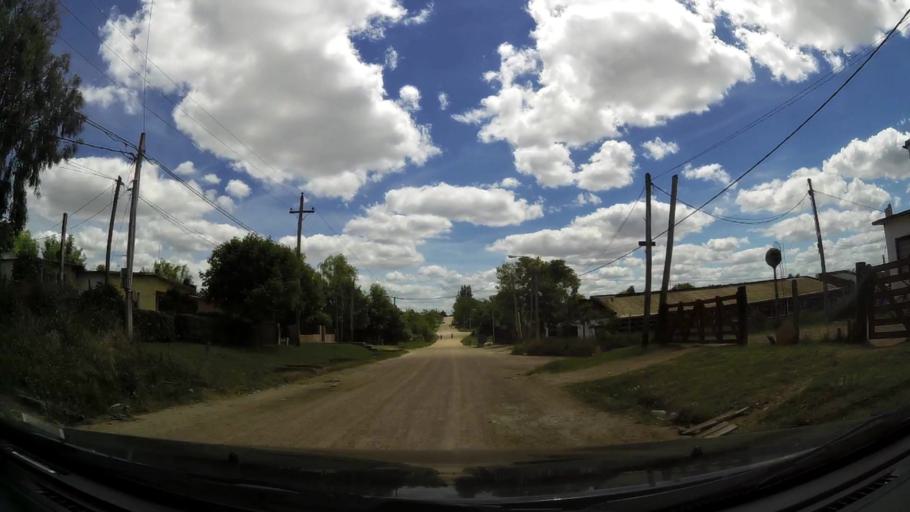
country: UY
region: Canelones
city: Colonia Nicolich
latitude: -34.7914
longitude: -55.9983
